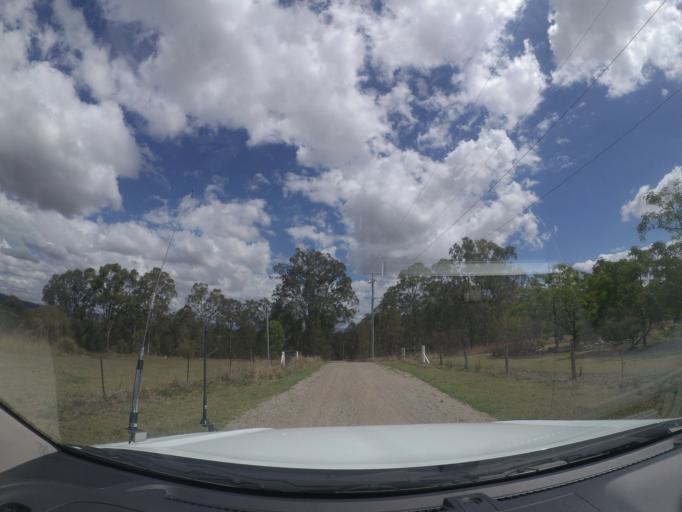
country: AU
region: Queensland
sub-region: Logan
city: Cedar Vale
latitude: -27.8967
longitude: 153.0012
